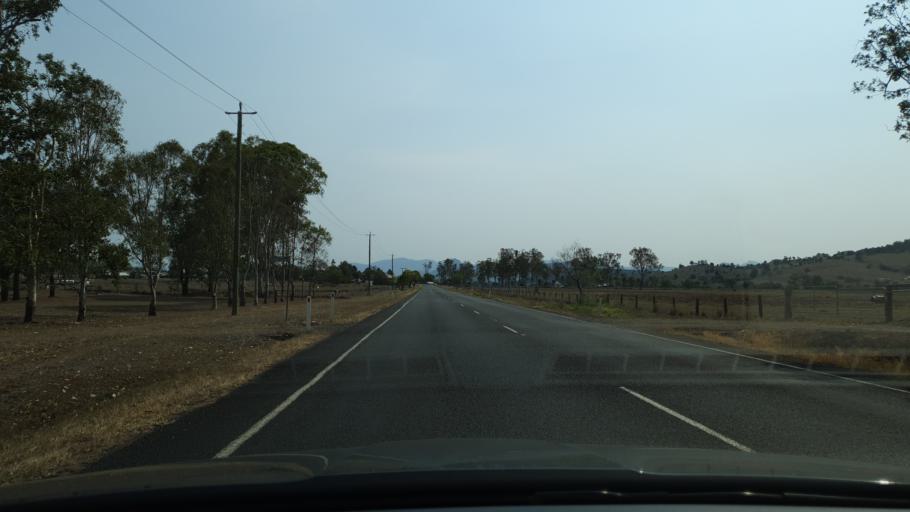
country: AU
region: Queensland
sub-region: Ipswich
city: Deebing Heights
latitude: -28.0135
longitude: 152.6753
